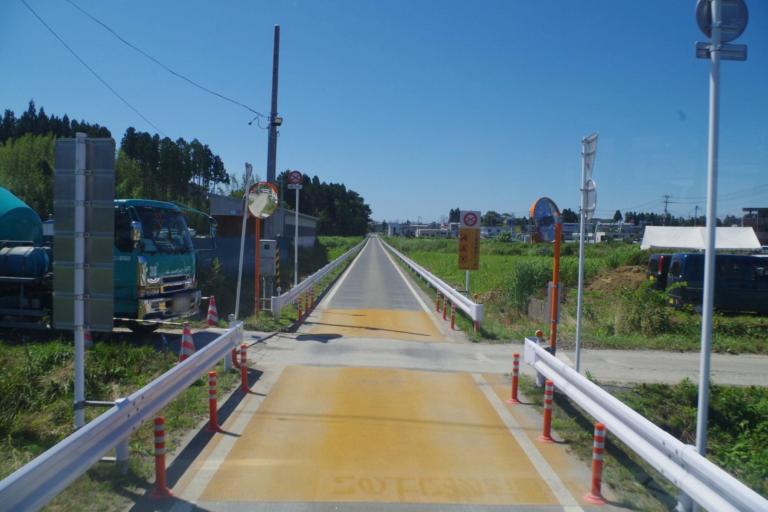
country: JP
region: Iwate
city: Ofunato
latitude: 38.8443
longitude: 141.5818
